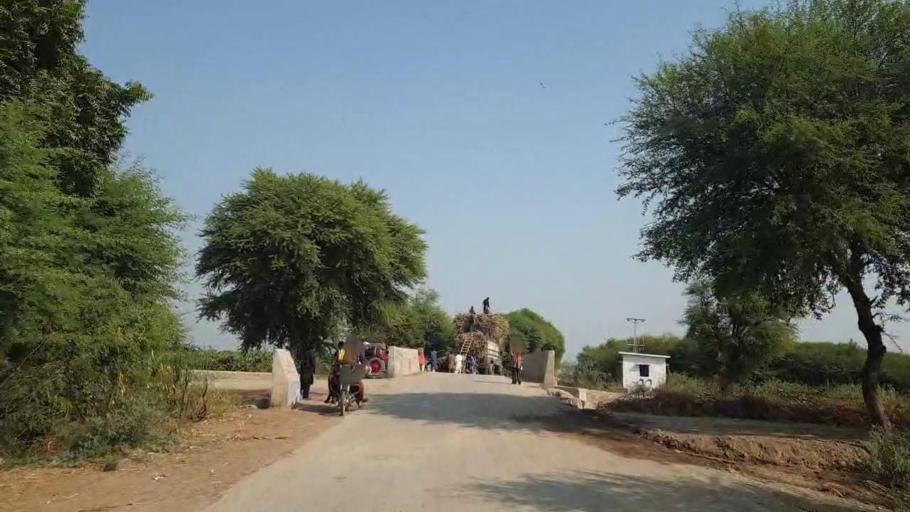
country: PK
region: Sindh
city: Matiari
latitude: 25.5017
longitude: 68.4475
